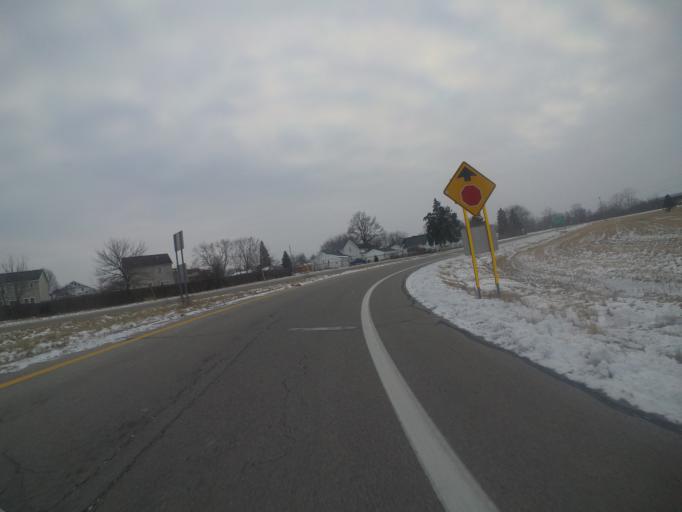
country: US
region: Ohio
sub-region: Wood County
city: Walbridge
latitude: 41.5638
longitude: -83.5090
